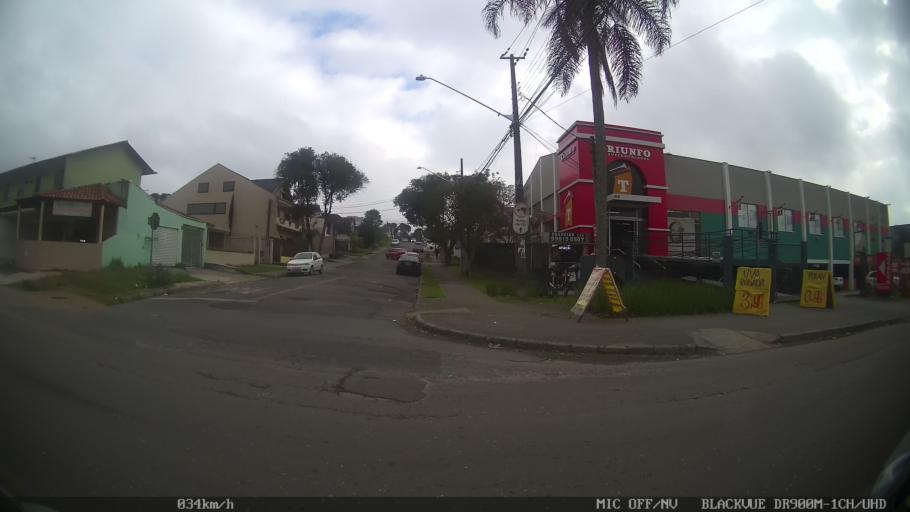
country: BR
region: Parana
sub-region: Curitiba
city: Curitiba
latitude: -25.3694
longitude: -49.2688
